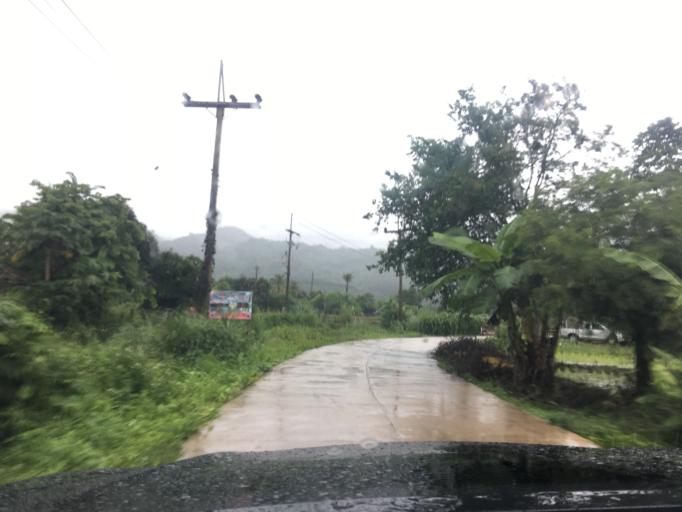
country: TH
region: Chiang Rai
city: Chiang Khong
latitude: 20.2989
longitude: 100.2558
